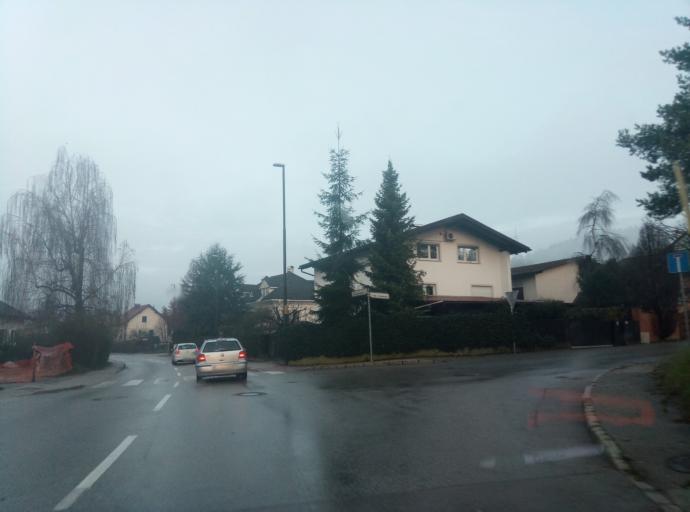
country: SI
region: Trzin
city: Trzin
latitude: 46.1079
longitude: 14.5326
